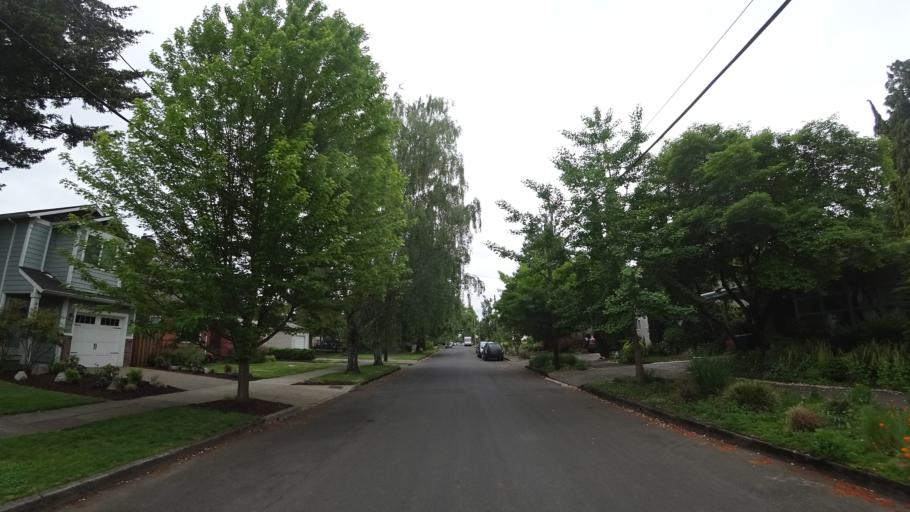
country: US
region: Oregon
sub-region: Clackamas County
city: Milwaukie
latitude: 45.4865
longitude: -122.6154
